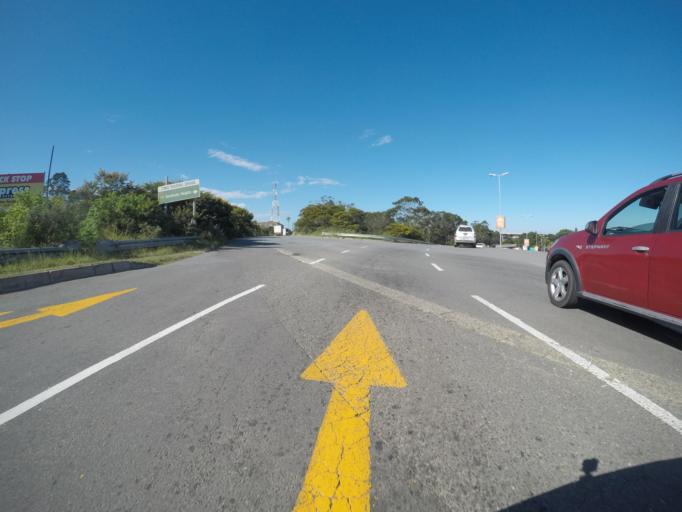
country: ZA
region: Eastern Cape
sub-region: Buffalo City Metropolitan Municipality
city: East London
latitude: -32.9699
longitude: 27.8959
